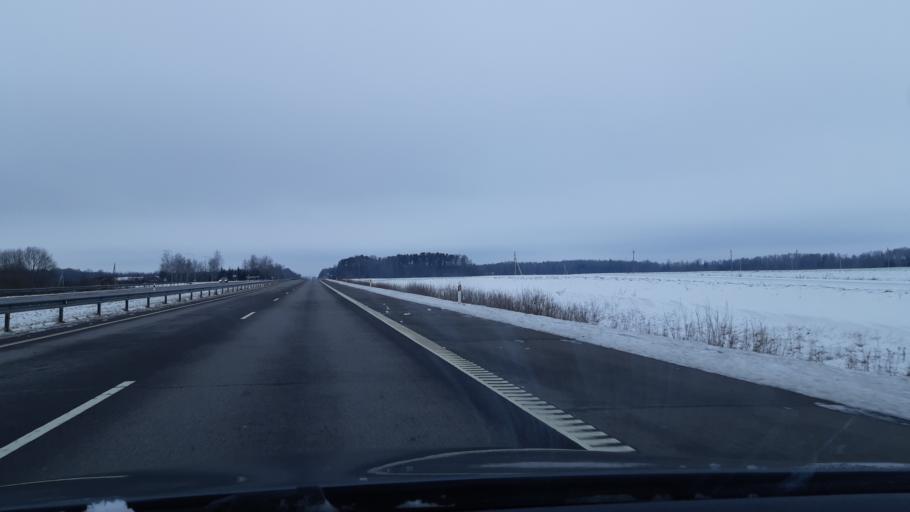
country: LT
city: Vilkija
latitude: 55.1215
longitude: 23.7549
